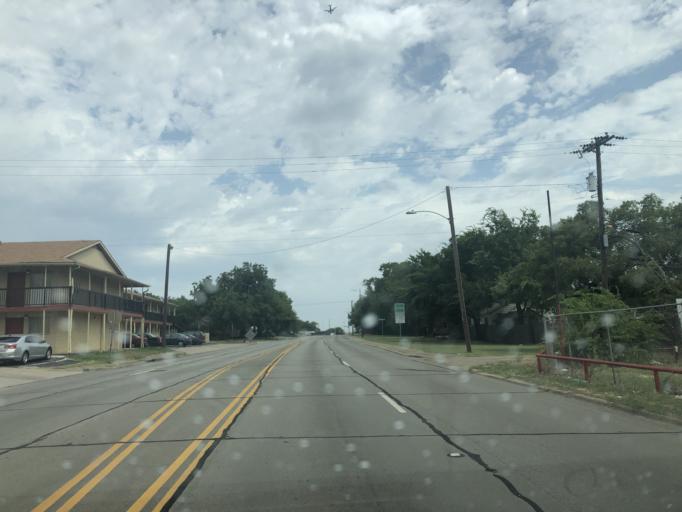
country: US
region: Texas
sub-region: Dallas County
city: Grand Prairie
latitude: 32.7411
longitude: -97.0291
